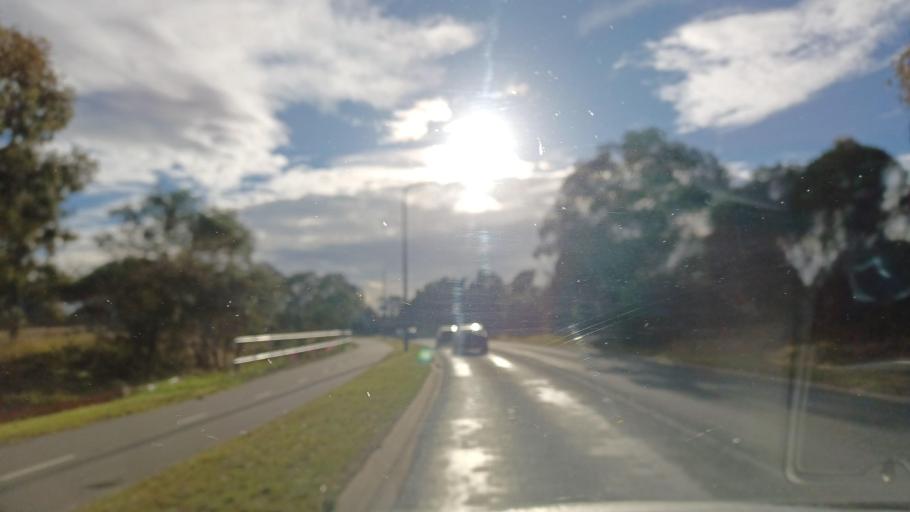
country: AU
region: Australian Capital Territory
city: Belconnen
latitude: -35.1920
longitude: 149.0699
